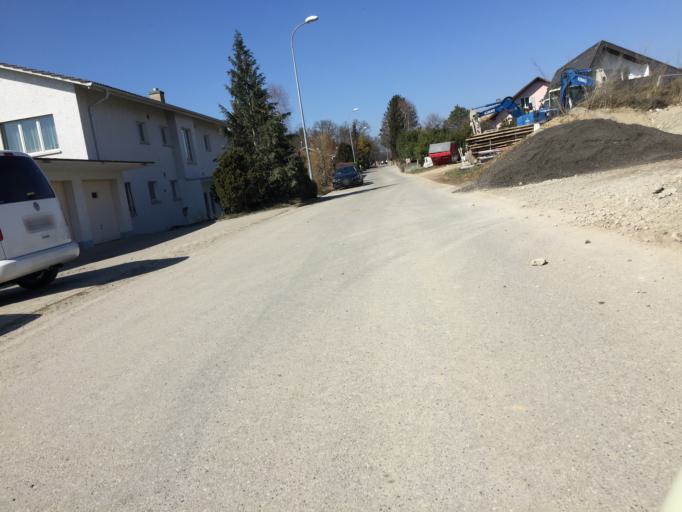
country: CH
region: Bern
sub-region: Bern-Mittelland District
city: Munsingen
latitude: 46.8820
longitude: 7.5682
